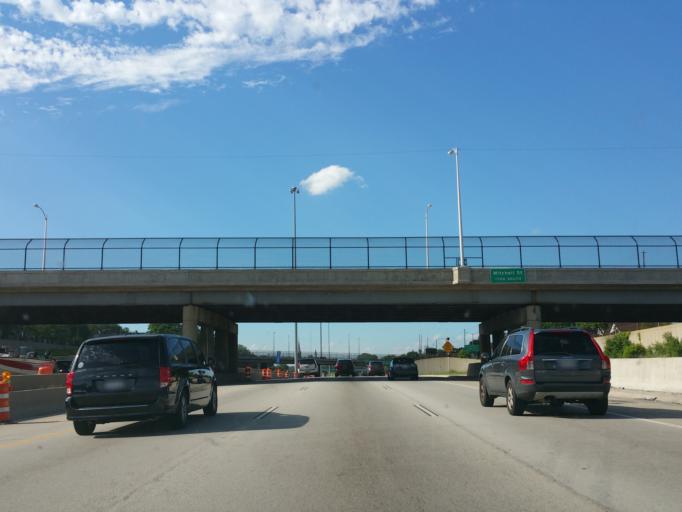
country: US
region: Wisconsin
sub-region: Milwaukee County
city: Milwaukee
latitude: 43.0116
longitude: -87.9160
